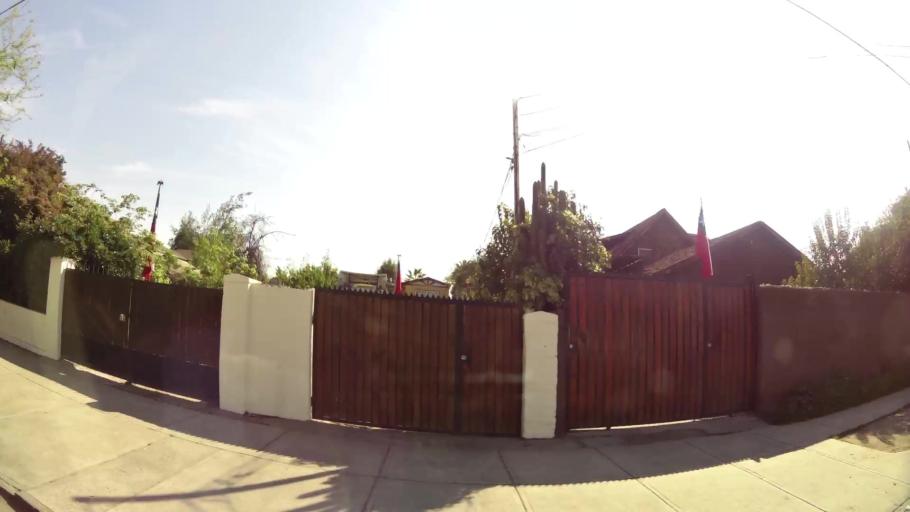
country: CL
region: Santiago Metropolitan
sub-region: Provincia de Maipo
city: San Bernardo
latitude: -33.5573
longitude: -70.6714
